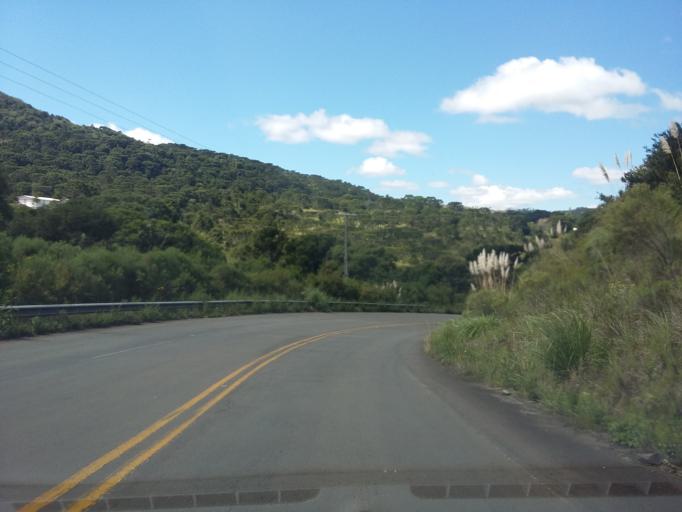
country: BR
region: Santa Catarina
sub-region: Sao Joaquim
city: Sao Joaquim
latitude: -28.2591
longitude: -49.7620
